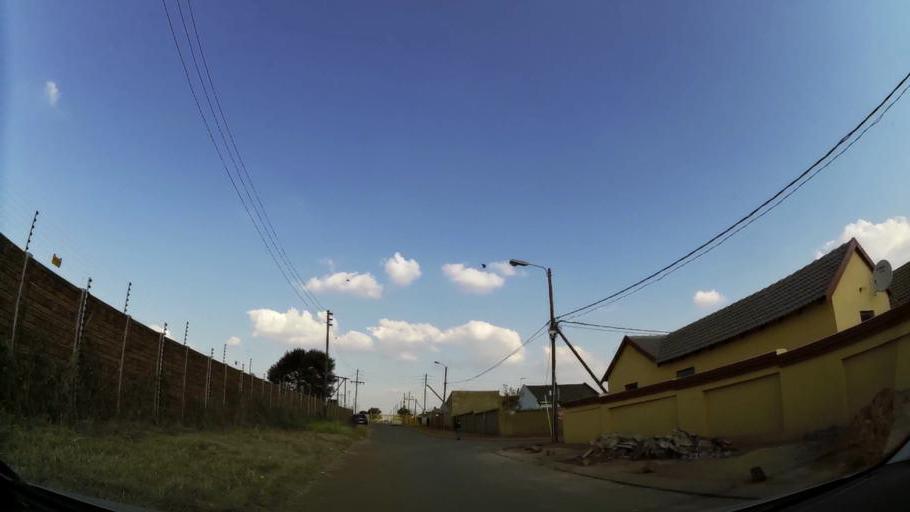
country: ZA
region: Gauteng
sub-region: Ekurhuleni Metropolitan Municipality
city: Tembisa
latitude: -25.9506
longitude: 28.2125
